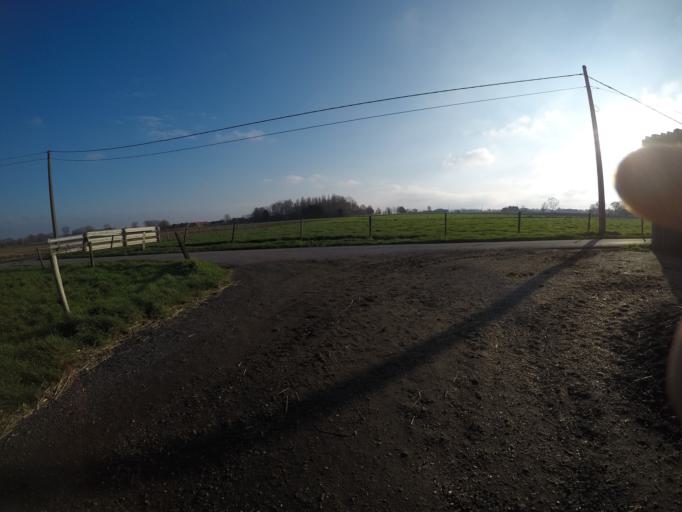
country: BE
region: Flanders
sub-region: Provincie West-Vlaanderen
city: Lichtervelde
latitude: 51.0539
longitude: 3.1904
